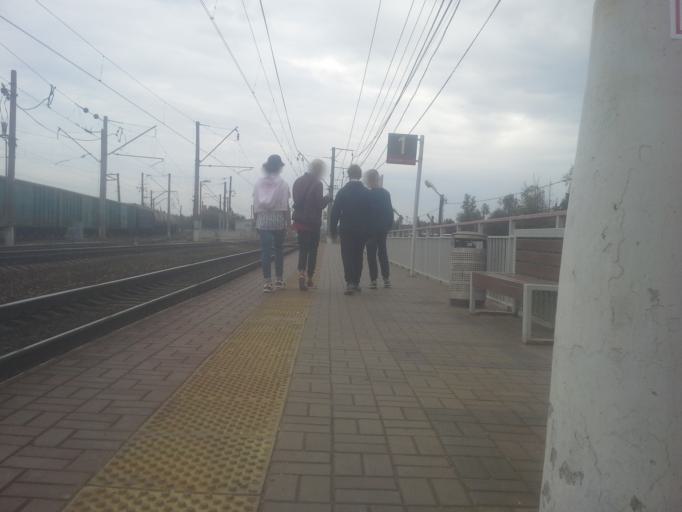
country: RU
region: Moskovskaya
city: Kievskij
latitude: 55.4253
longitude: 36.8651
